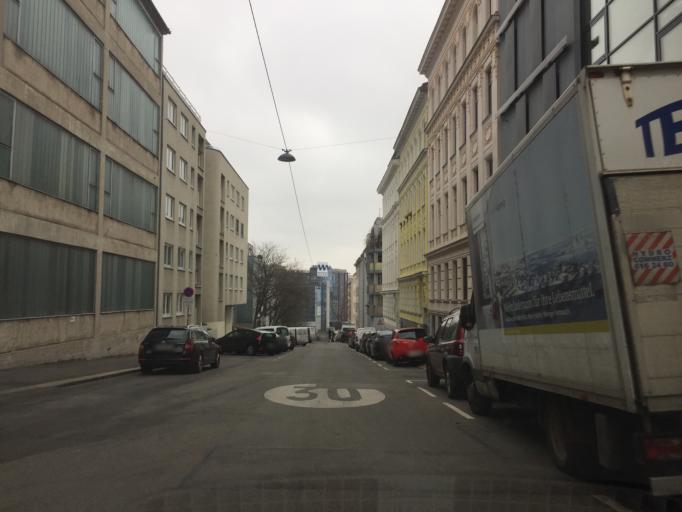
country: AT
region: Lower Austria
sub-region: Politischer Bezirk Modling
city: Perchtoldsdorf
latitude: 48.1965
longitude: 16.2904
